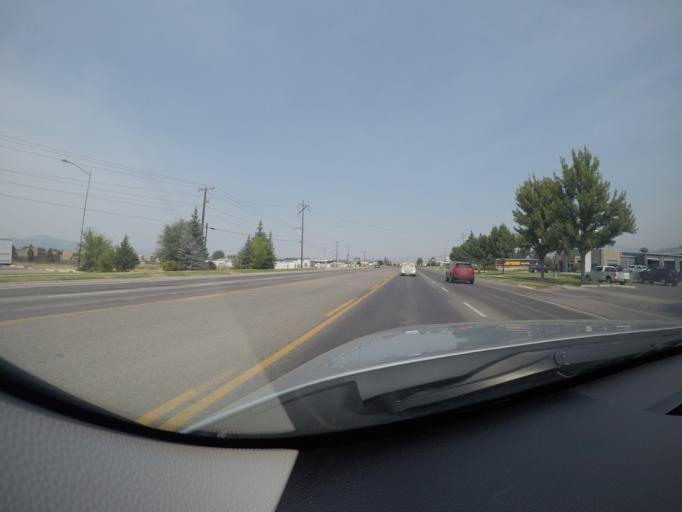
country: US
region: Montana
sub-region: Missoula County
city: Missoula
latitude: 46.8826
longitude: -114.0232
